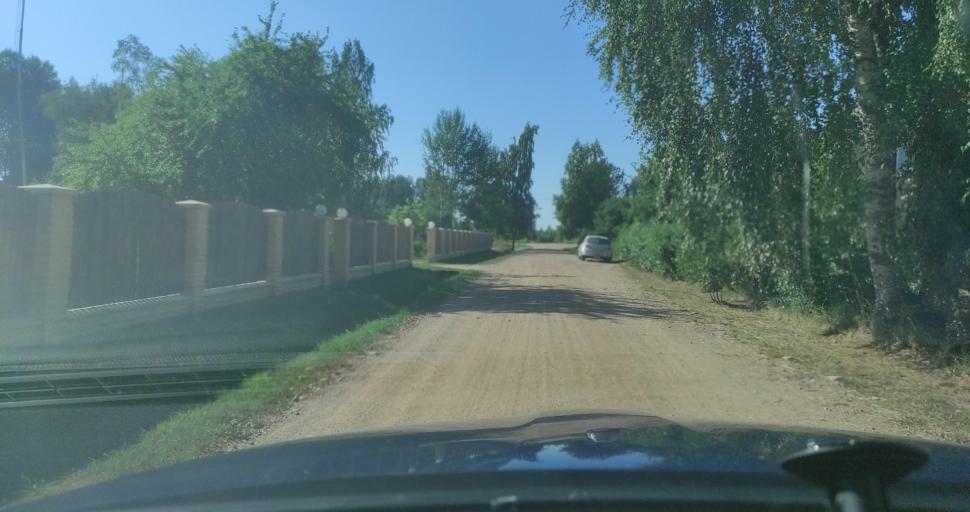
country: LV
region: Skrunda
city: Skrunda
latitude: 56.6767
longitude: 22.0076
